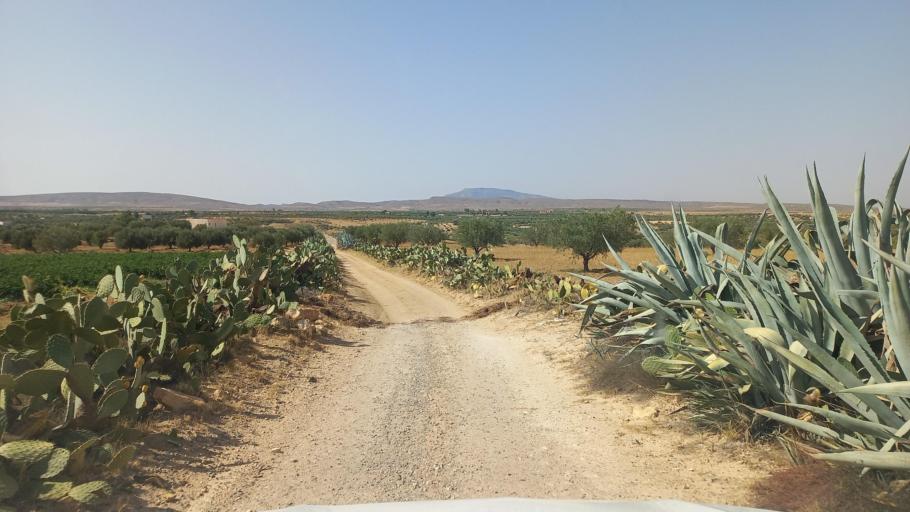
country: TN
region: Al Qasrayn
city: Kasserine
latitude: 35.2311
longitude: 9.0510
